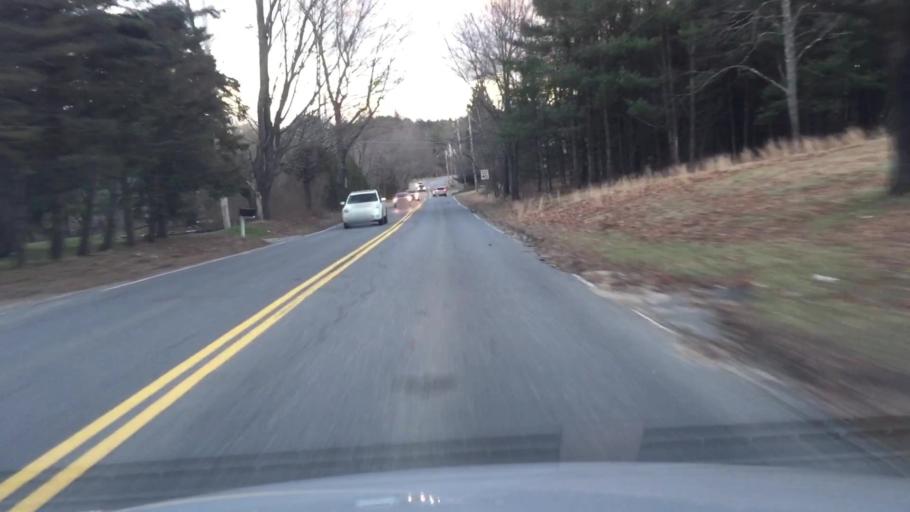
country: US
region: Massachusetts
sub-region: Worcester County
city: Sterling
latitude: 42.4176
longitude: -71.8042
